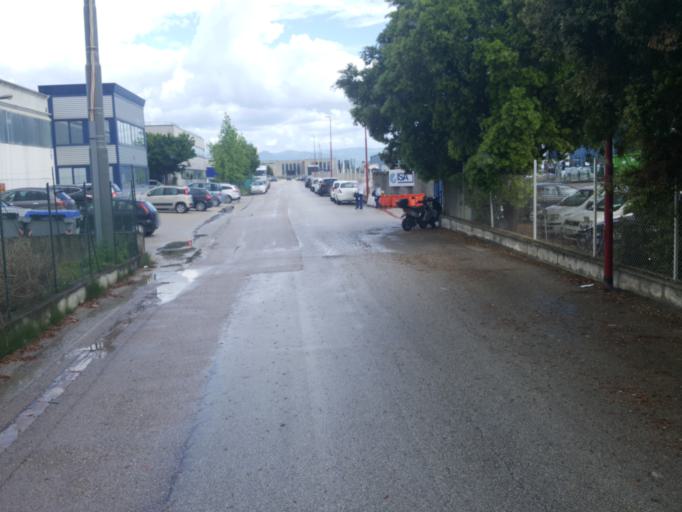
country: IT
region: Umbria
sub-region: Provincia di Perugia
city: Bastia umbra
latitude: 43.0527
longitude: 12.5474
